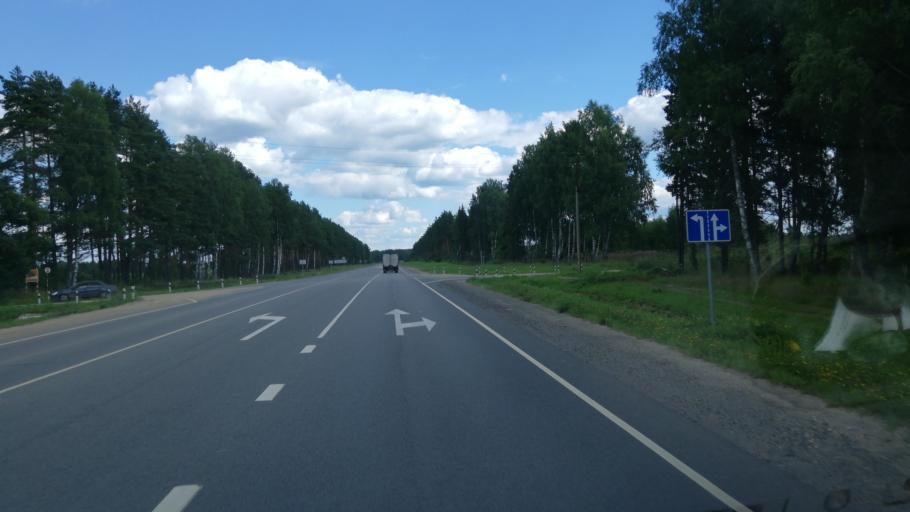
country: RU
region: Jaroslavl
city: Levashevo
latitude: 57.6419
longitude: 40.4887
